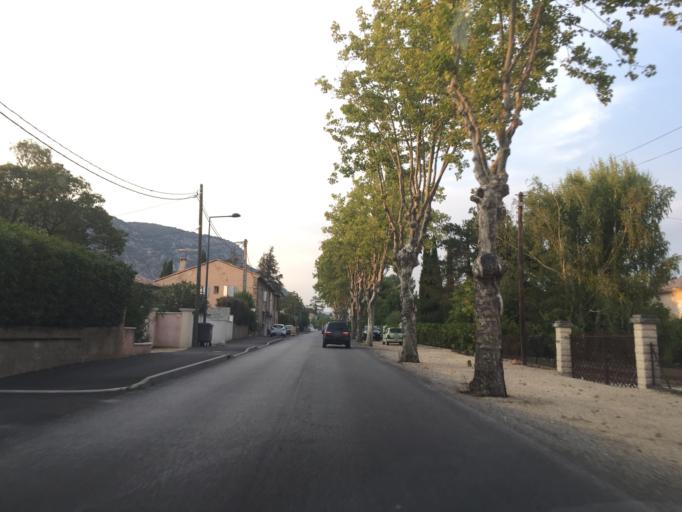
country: FR
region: Provence-Alpes-Cote d'Azur
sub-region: Departement des Alpes-de-Haute-Provence
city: Volx
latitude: 43.8723
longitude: 5.8434
